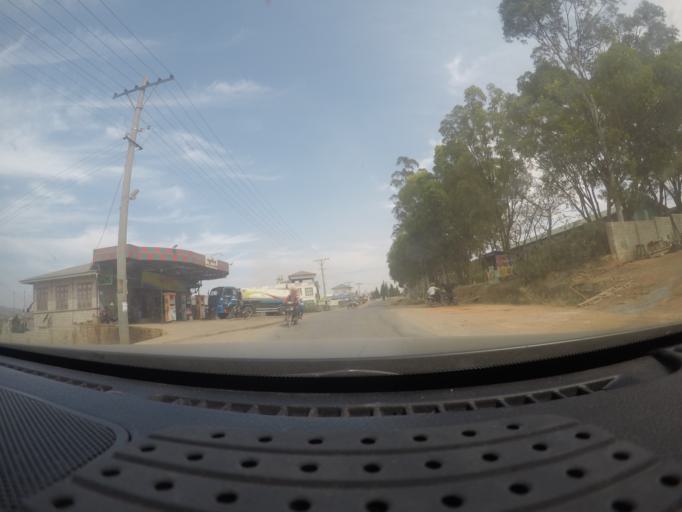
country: MM
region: Shan
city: Taunggyi
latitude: 20.6741
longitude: 96.6314
